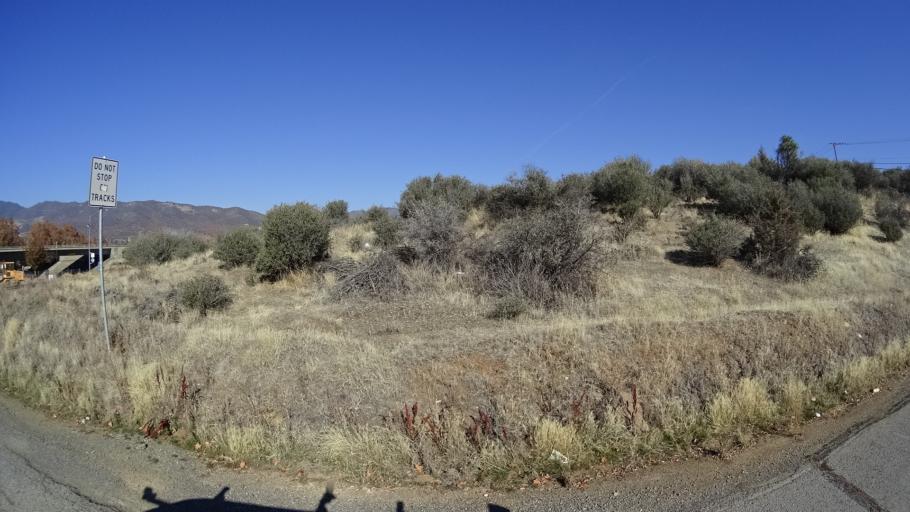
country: US
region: California
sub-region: Siskiyou County
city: Yreka
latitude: 41.7303
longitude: -122.6319
